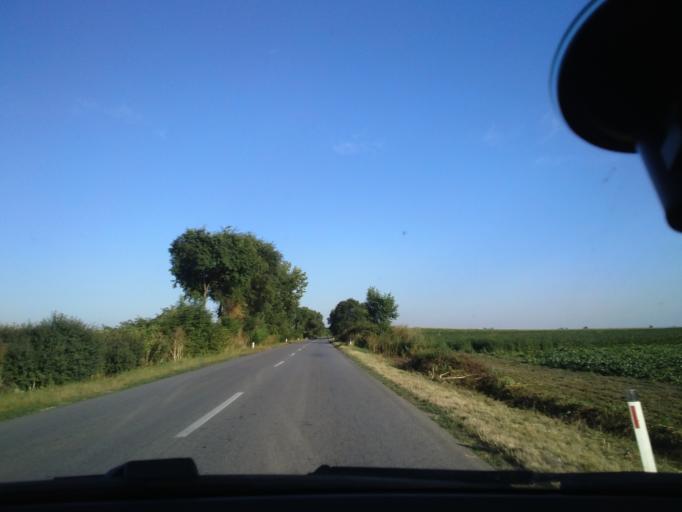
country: RS
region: Autonomna Pokrajina Vojvodina
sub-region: Zapadnobacki Okrug
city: Odzaci
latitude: 45.4708
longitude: 19.3045
